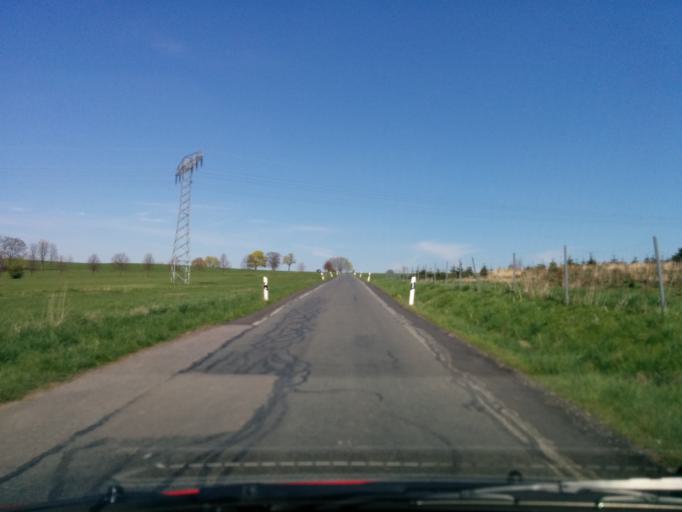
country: DE
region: Saxony
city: Niederwiesa
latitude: 50.8358
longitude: 13.0312
